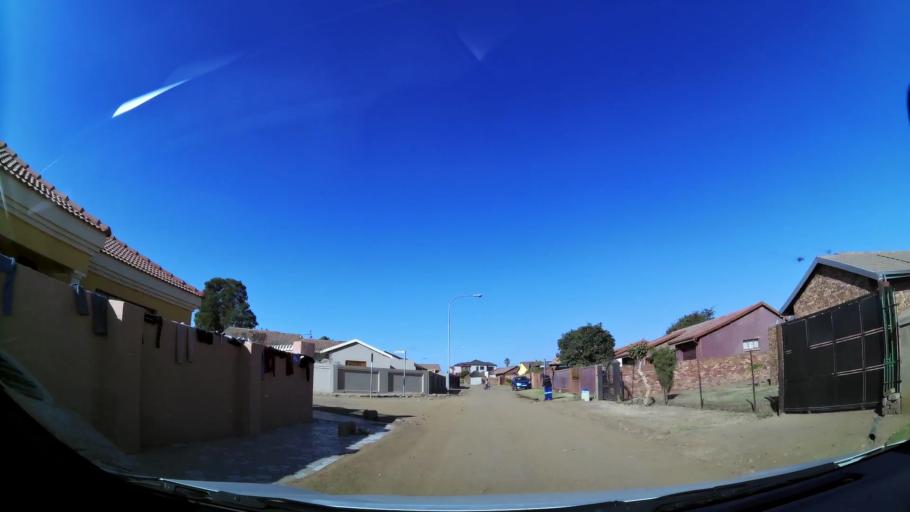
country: ZA
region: Gauteng
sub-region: City of Tshwane Metropolitan Municipality
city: Cullinan
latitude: -25.7175
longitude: 28.3881
